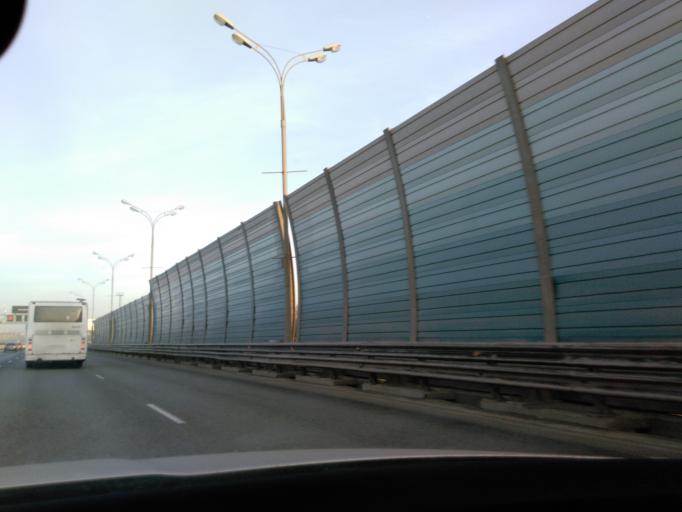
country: RU
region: Moscow
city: Luzhniki
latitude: 55.7185
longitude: 37.5673
